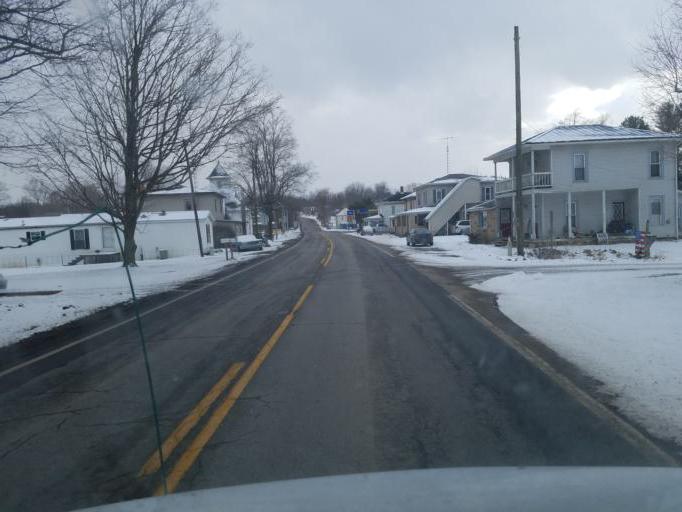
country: US
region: Ohio
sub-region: Holmes County
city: Millersburg
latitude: 40.4505
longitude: -81.9020
